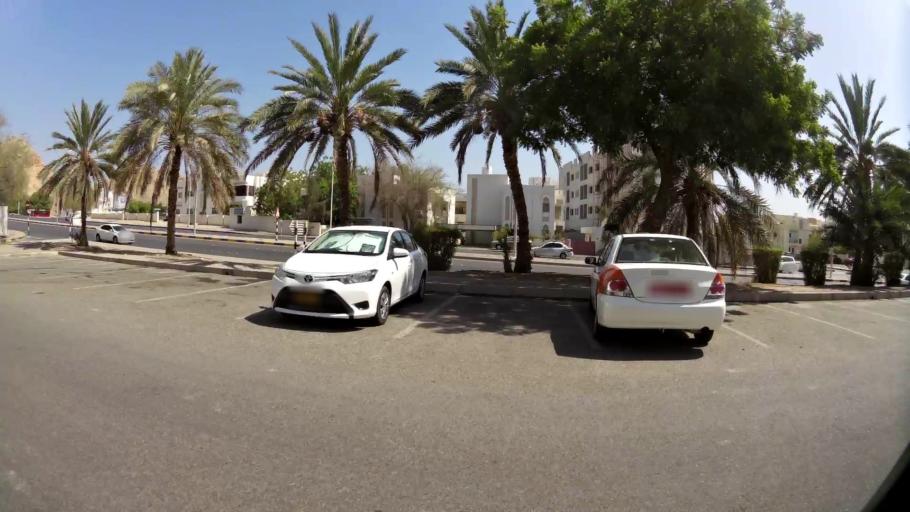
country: OM
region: Muhafazat Masqat
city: Muscat
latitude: 23.6033
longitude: 58.5383
